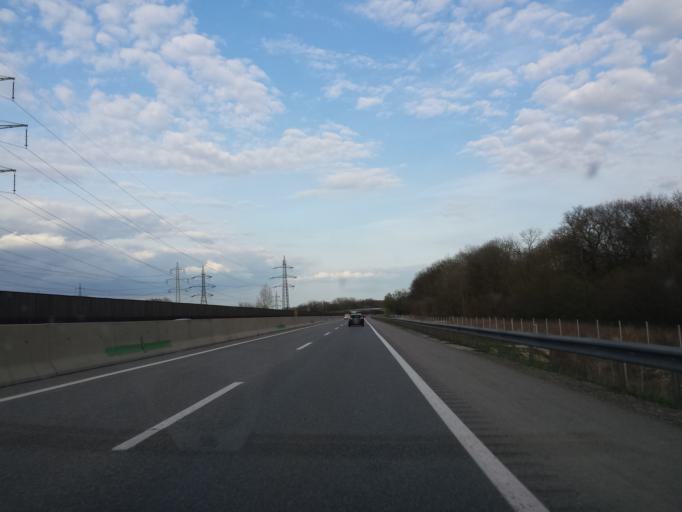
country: AT
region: Lower Austria
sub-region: Politischer Bezirk Korneuburg
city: Sierndorf
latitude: 48.3766
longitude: 16.1469
